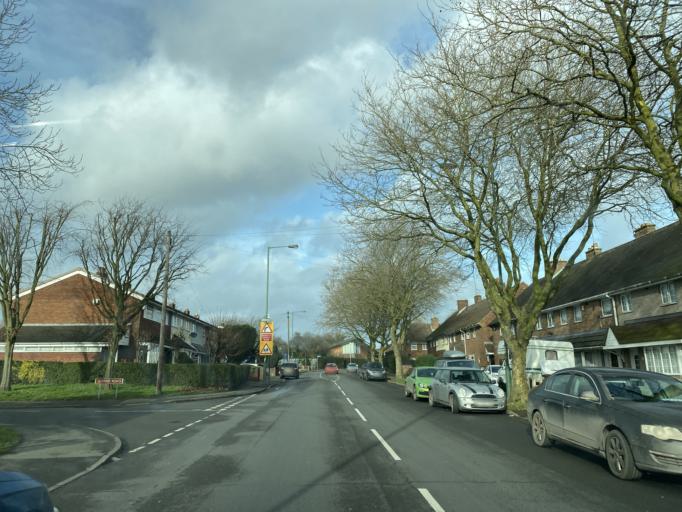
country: GB
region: England
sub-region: Walsall
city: Bloxwich
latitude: 52.6038
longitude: -2.0148
